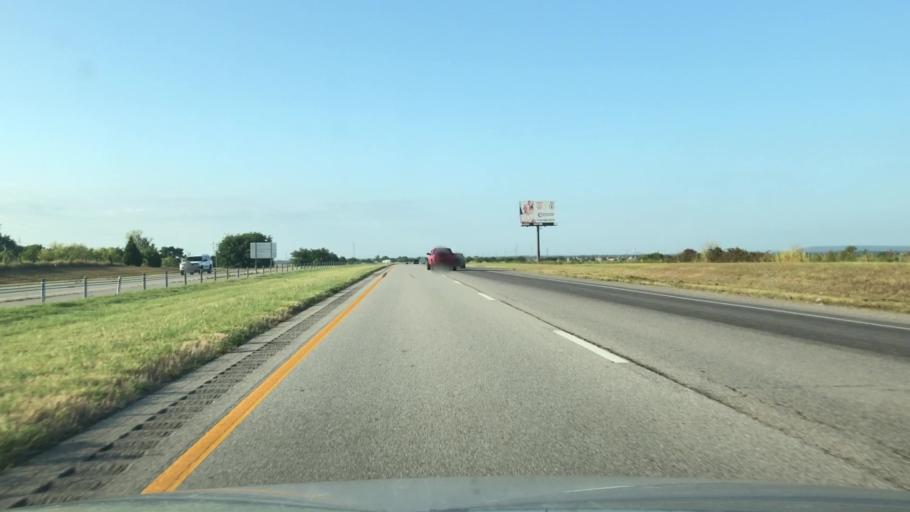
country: US
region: Oklahoma
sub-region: Osage County
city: Skiatook
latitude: 36.3619
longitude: -95.9208
